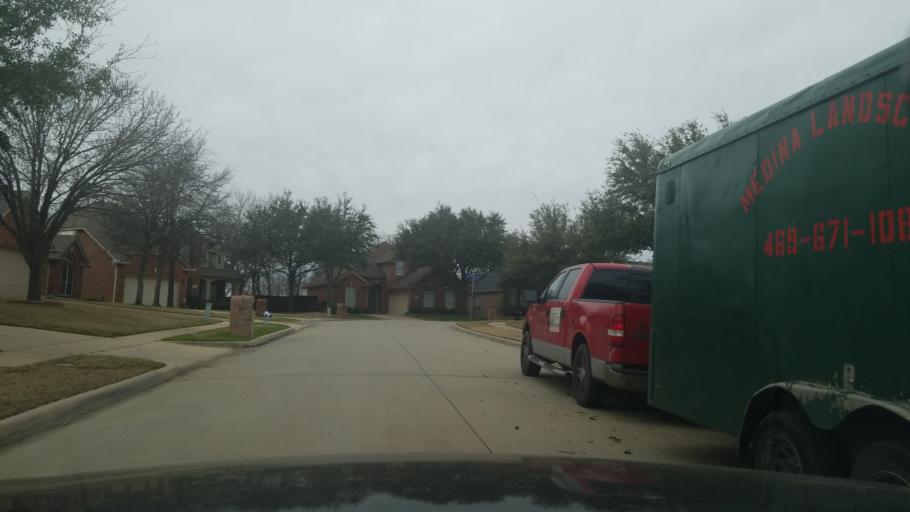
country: US
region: Texas
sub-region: Denton County
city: Corinth
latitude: 33.1311
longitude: -97.0755
